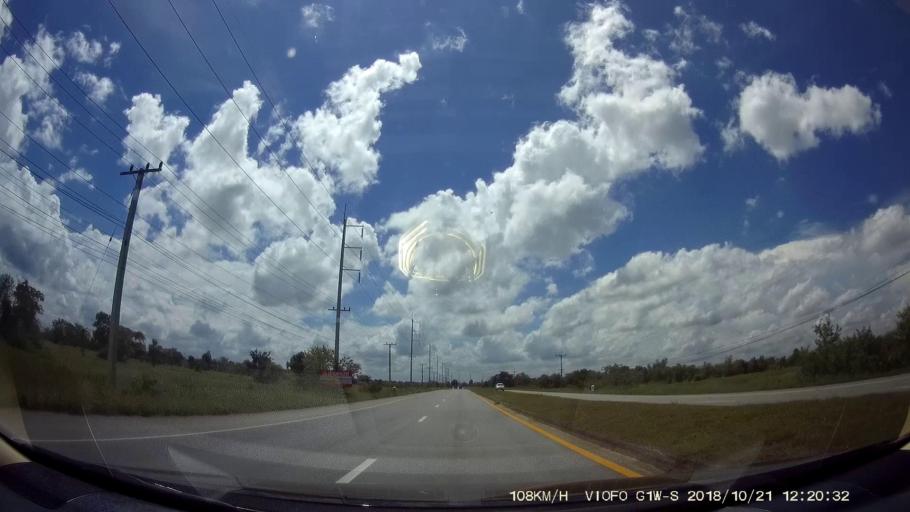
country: TH
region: Nakhon Ratchasima
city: Dan Khun Thot
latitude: 15.2864
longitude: 101.8021
